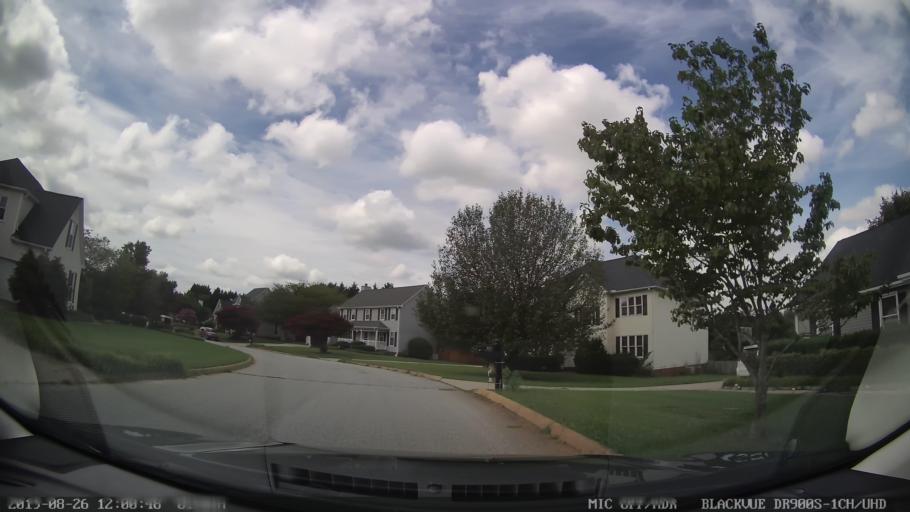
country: US
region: South Carolina
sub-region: Greenville County
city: Five Forks
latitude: 34.8005
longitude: -82.2358
